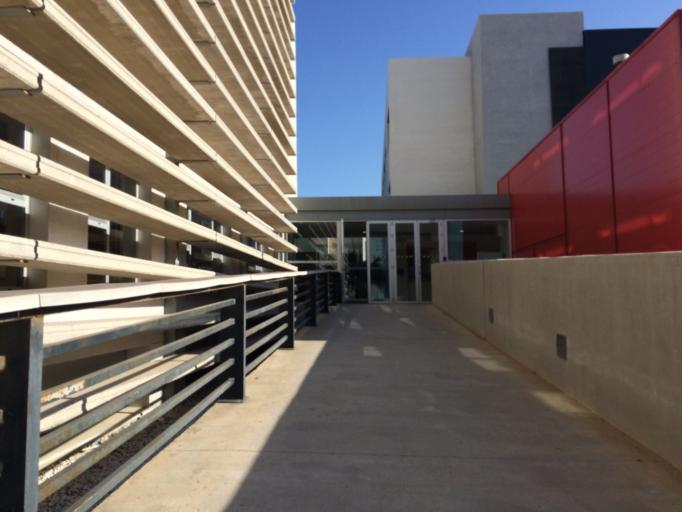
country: ES
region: Andalusia
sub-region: Provincia de Almeria
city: Almeria
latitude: 36.8300
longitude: -2.4075
